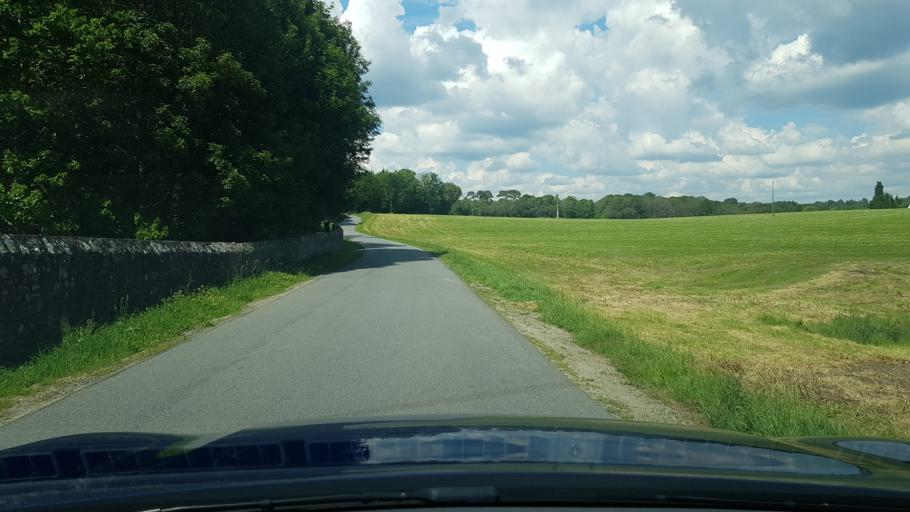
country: FR
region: Brittany
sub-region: Departement du Morbihan
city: Guidel-Plage
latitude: 47.8014
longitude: -3.4988
